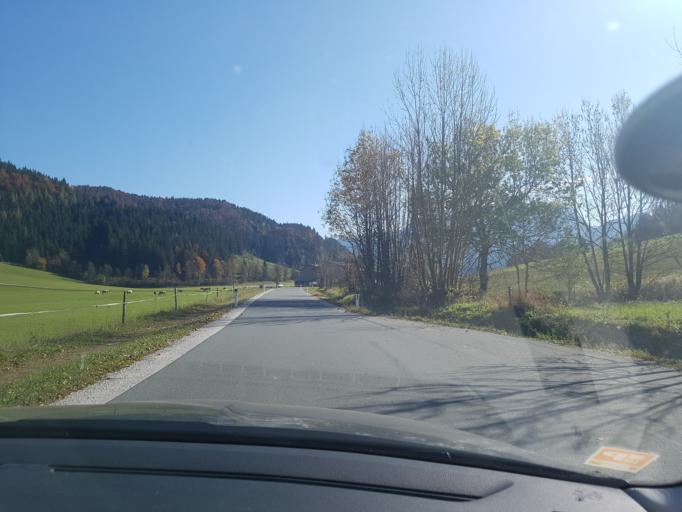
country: AT
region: Tyrol
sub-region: Politischer Bezirk Kitzbuhel
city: Hochfilzen
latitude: 47.4862
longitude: 12.6104
